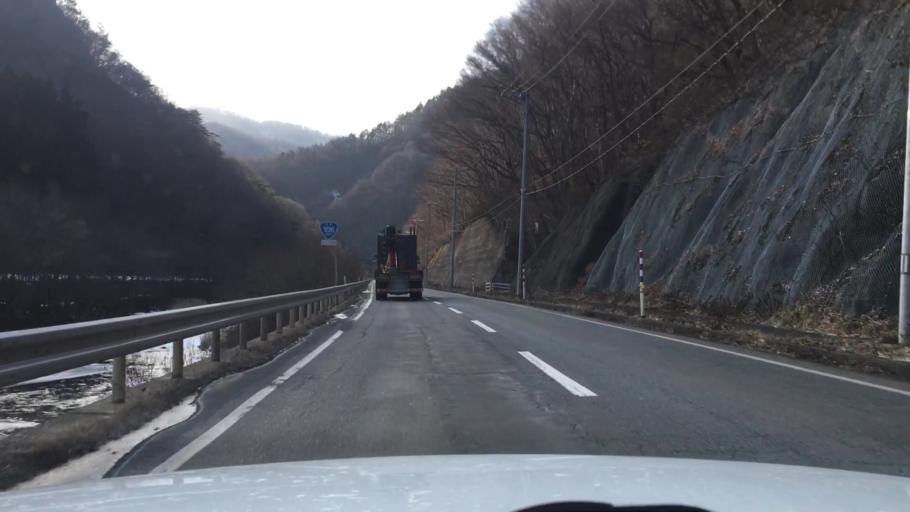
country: JP
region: Iwate
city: Tono
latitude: 39.6494
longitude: 141.5777
